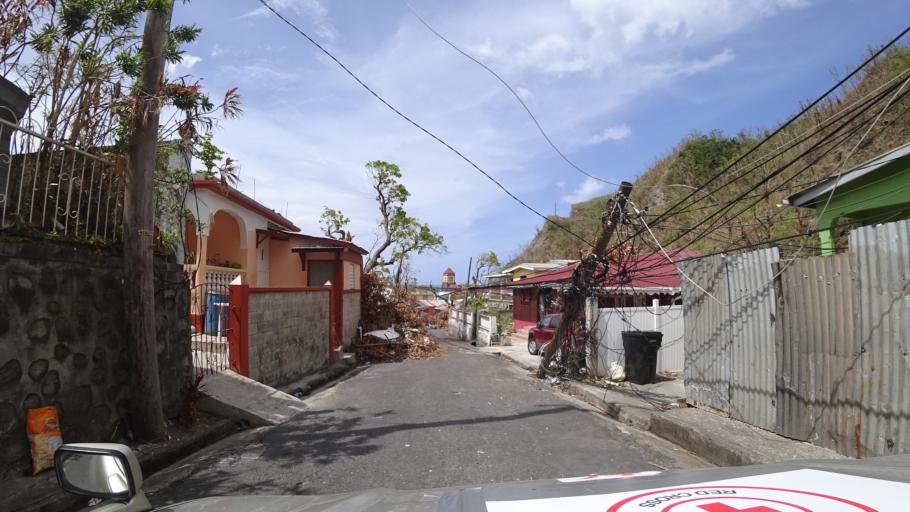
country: DM
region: Saint Mark
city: Soufriere
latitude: 15.2335
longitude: -61.3602
